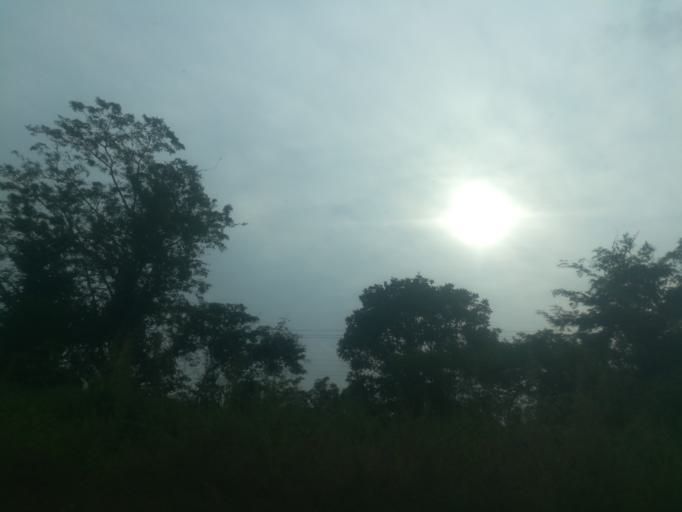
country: NG
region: Ogun
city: Ayetoro
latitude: 7.2321
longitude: 3.1361
